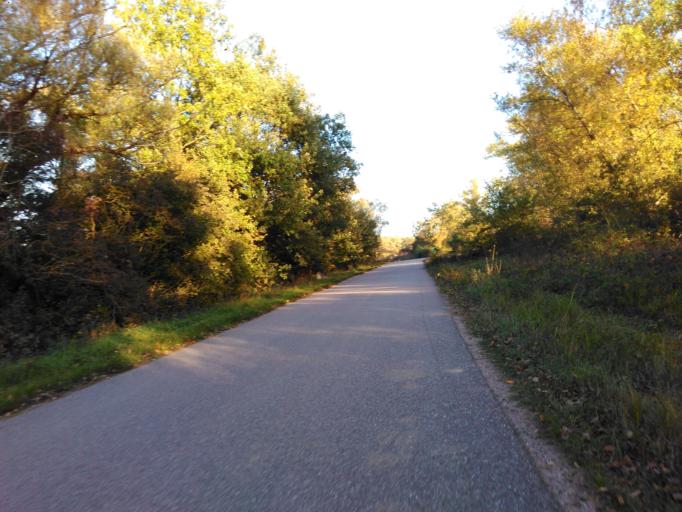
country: FR
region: Lorraine
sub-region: Departement de la Moselle
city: Argancy
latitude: 49.1946
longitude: 6.1901
